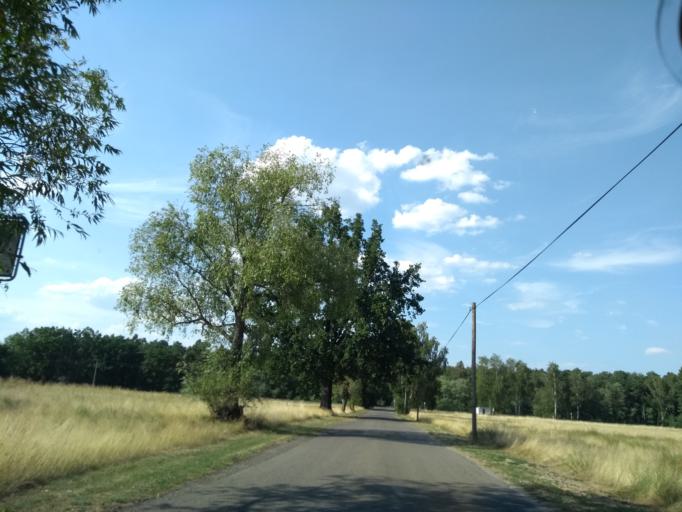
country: DE
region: Brandenburg
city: Luebben
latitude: 51.8563
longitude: 13.8499
